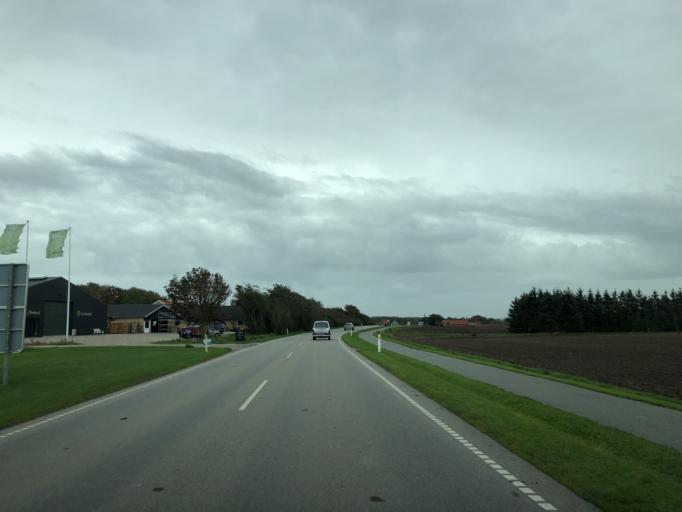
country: DK
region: North Denmark
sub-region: Thisted Kommune
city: Thisted
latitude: 56.9719
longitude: 8.6841
